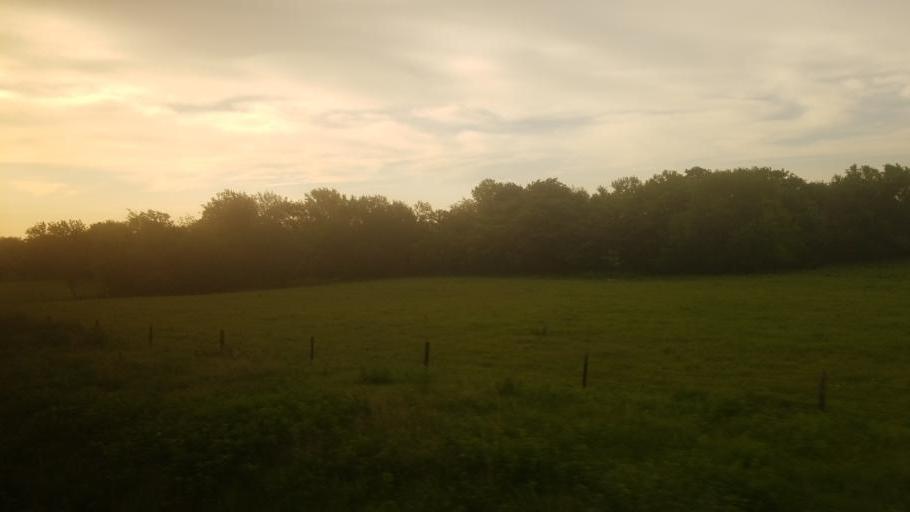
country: US
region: Kansas
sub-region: Lyon County
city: Emporia
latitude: 38.4819
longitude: -96.0485
